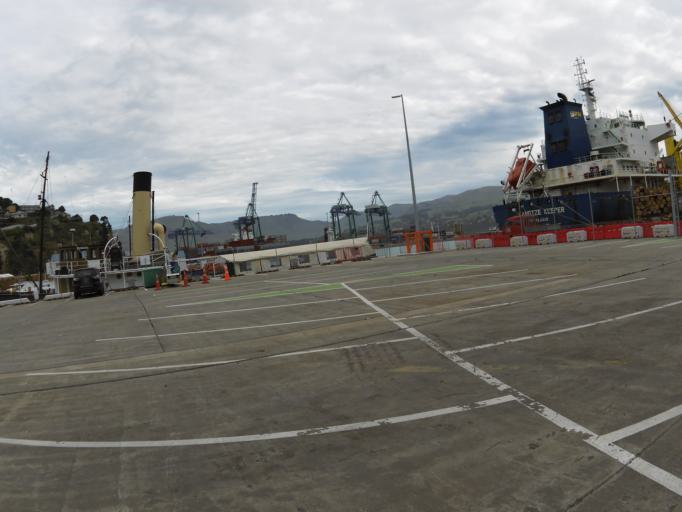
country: NZ
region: Canterbury
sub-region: Christchurch City
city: Christchurch
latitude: -43.6052
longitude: 172.7212
